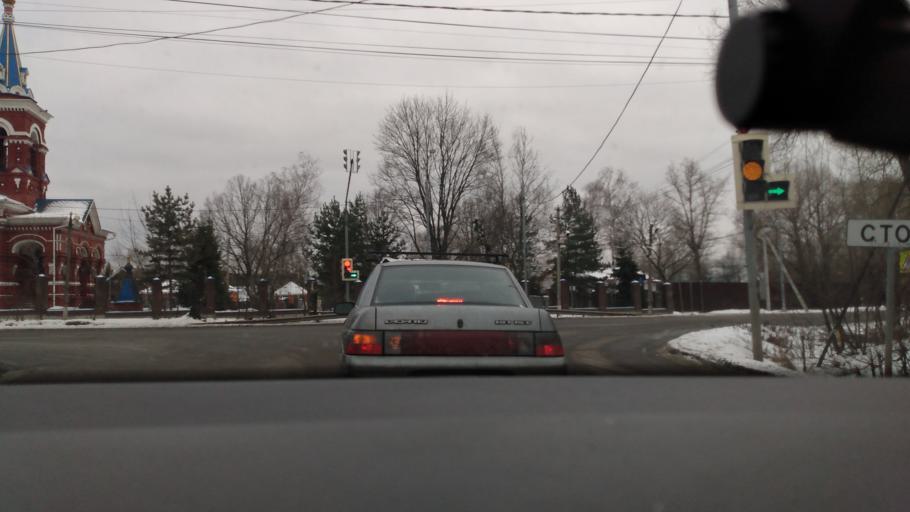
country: RU
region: Moskovskaya
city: Bykovo
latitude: 55.6565
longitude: 38.1012
